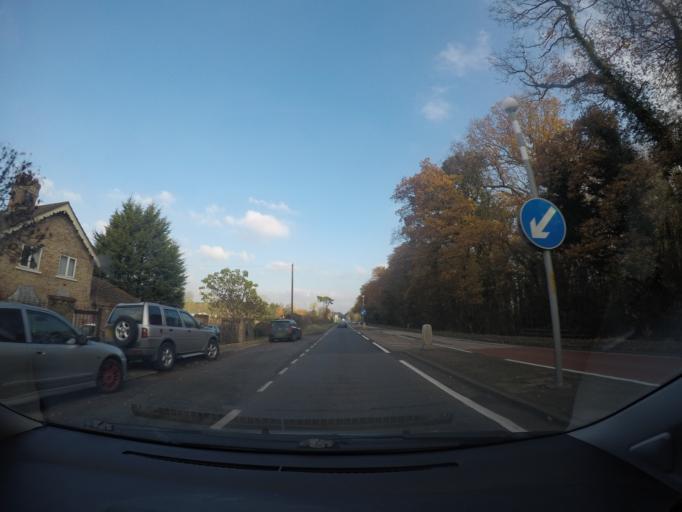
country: GB
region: England
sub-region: City of York
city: Holtby
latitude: 54.0136
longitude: -0.9887
